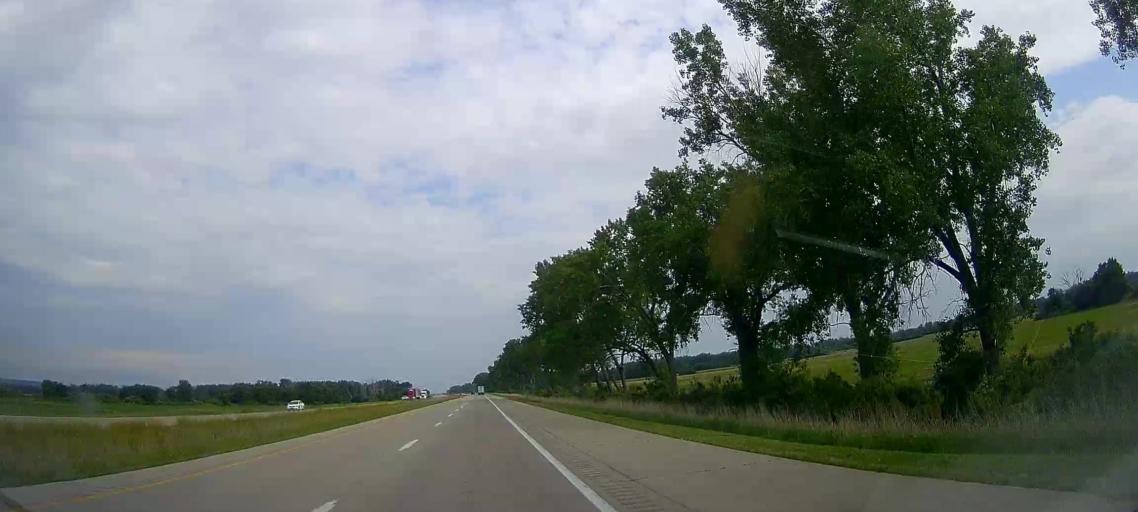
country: US
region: Nebraska
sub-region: Burt County
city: Tekamah
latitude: 41.8269
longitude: -96.0780
